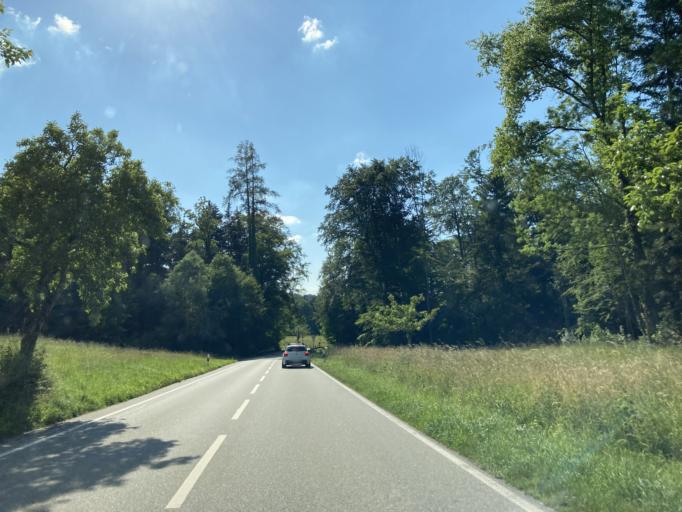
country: DE
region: Bavaria
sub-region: Upper Bavaria
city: Samerberg
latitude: 47.7897
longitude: 12.2379
